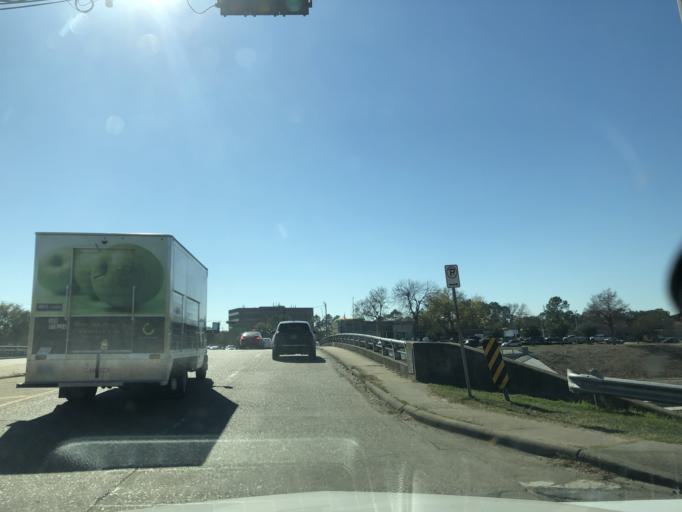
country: US
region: Texas
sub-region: Harris County
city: Bellaire
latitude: 29.6787
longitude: -95.4931
